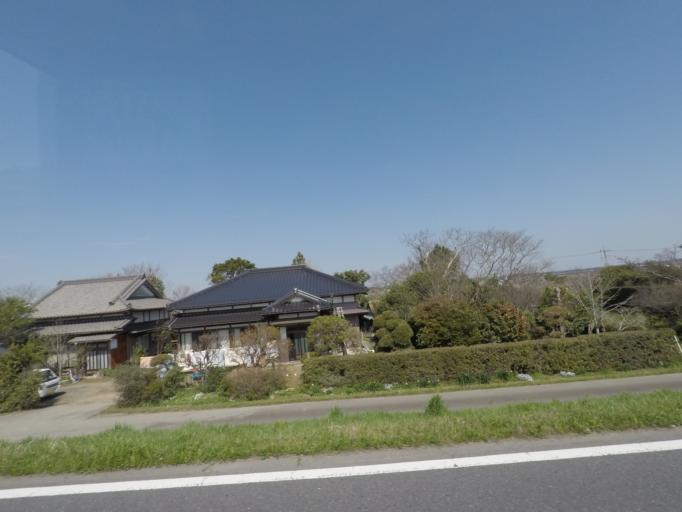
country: JP
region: Ibaraki
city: Edosaki
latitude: 35.8996
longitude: 140.3593
